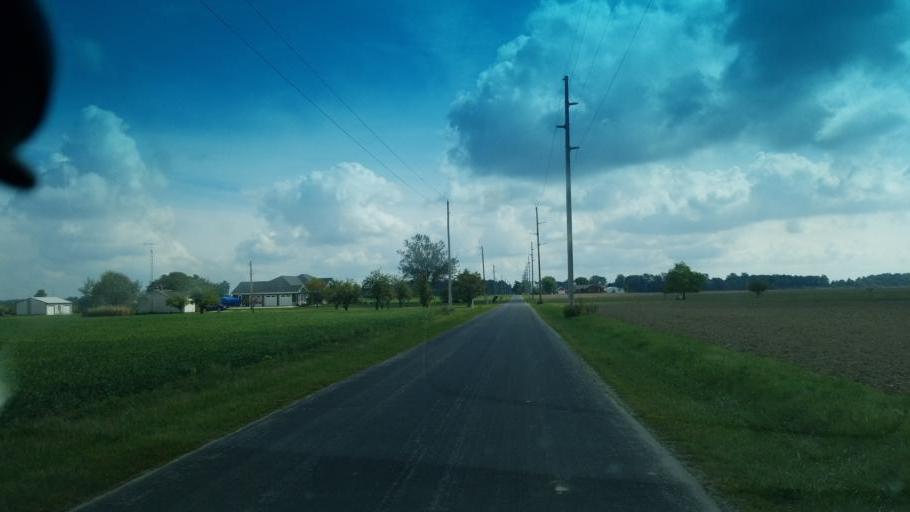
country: US
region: Ohio
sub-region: Wyandot County
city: Carey
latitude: 40.9343
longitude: -83.3746
